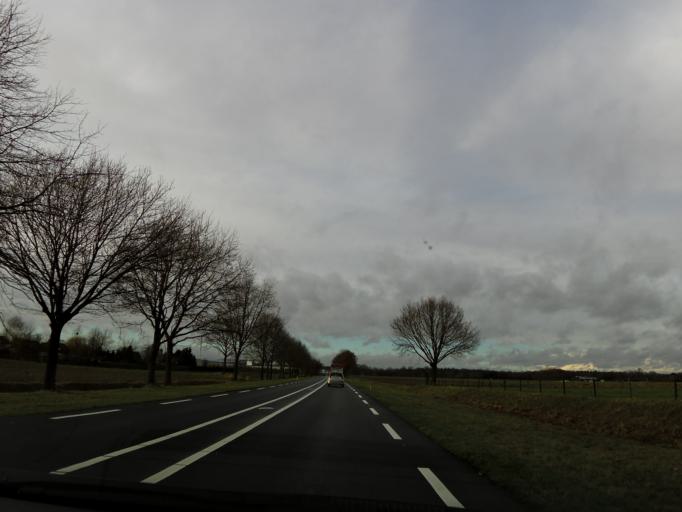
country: NL
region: Limburg
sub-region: Gemeente Roerdalen
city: Posterholt
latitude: 51.1270
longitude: 6.0363
